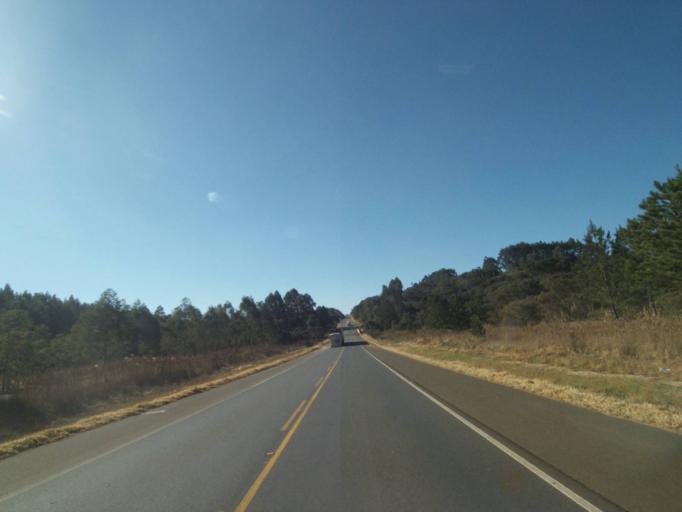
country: BR
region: Parana
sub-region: Tibagi
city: Tibagi
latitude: -24.6123
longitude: -50.4449
